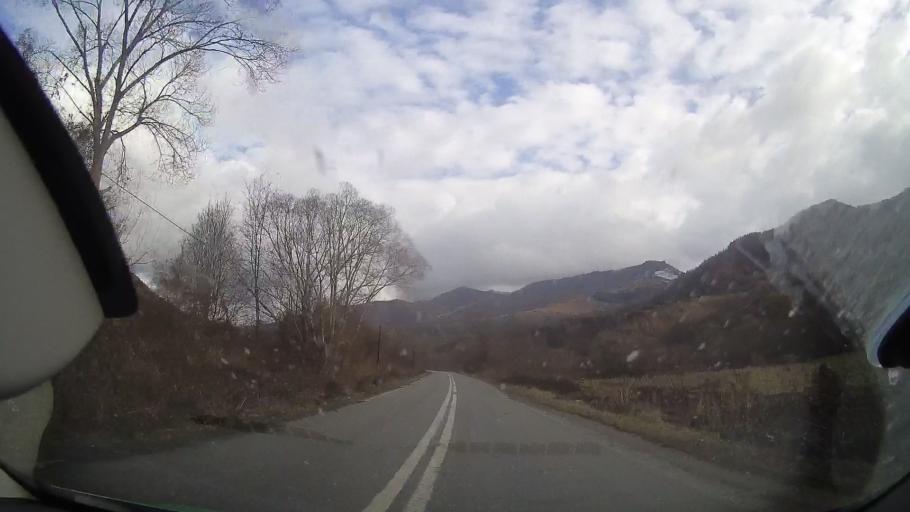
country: RO
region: Alba
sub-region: Comuna Ocolis
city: Ocolis
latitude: 46.4759
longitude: 23.5018
